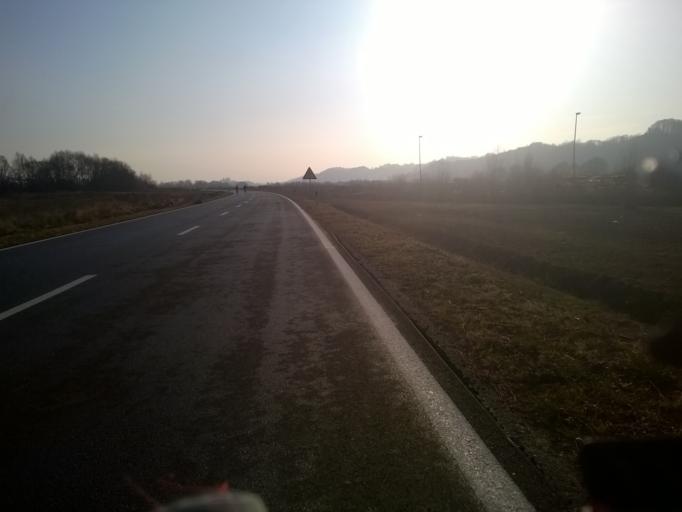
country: HR
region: Krapinsko-Zagorska
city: Zabok
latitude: 46.0678
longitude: 15.9135
